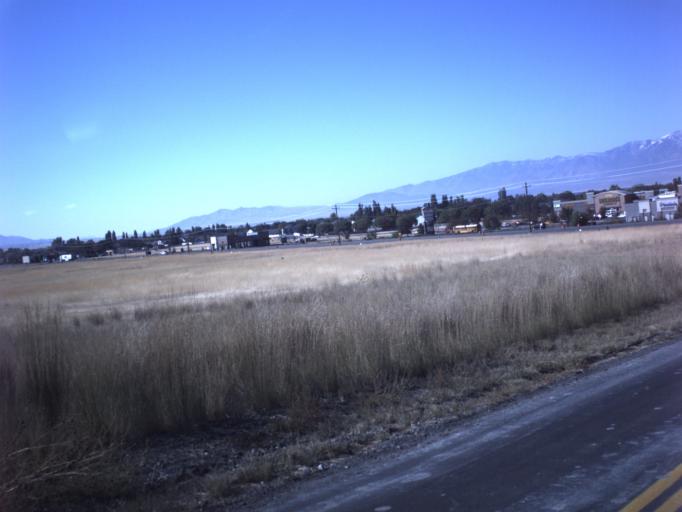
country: US
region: Utah
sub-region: Tooele County
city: Stansbury park
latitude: 40.6538
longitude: -112.2869
